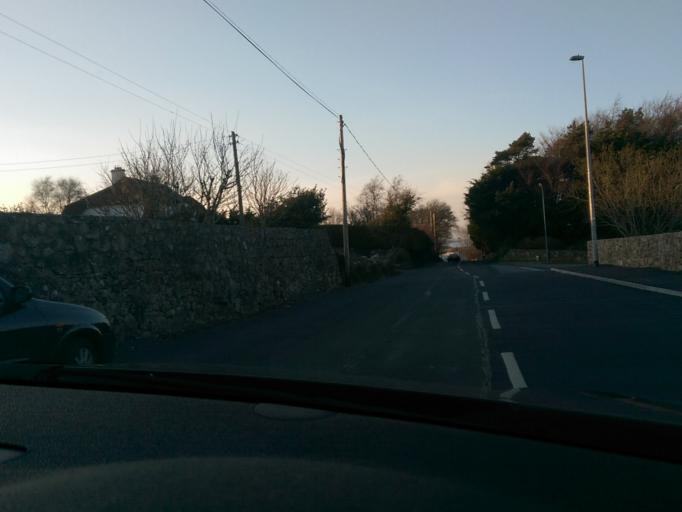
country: IE
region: Connaught
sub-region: County Galway
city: Gaillimh
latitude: 53.2873
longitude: -9.0821
